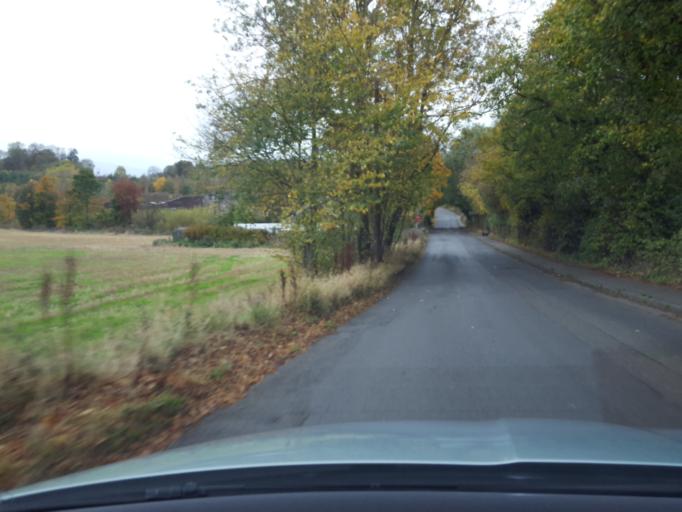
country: GB
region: Scotland
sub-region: Edinburgh
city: Ratho
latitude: 55.9256
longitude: -3.3804
